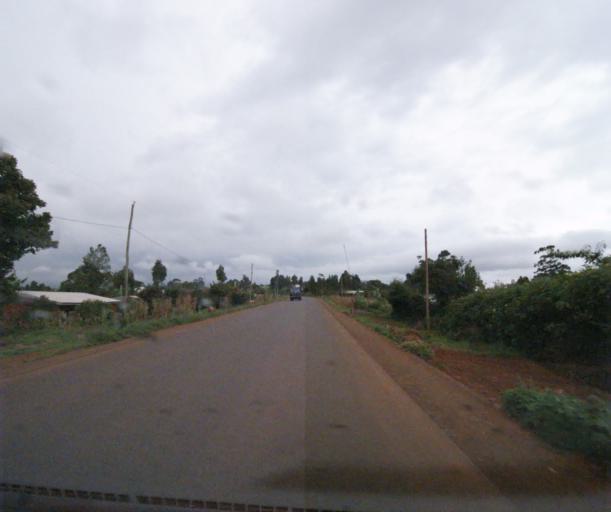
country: CM
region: West
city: Dschang
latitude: 5.4901
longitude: 10.1687
